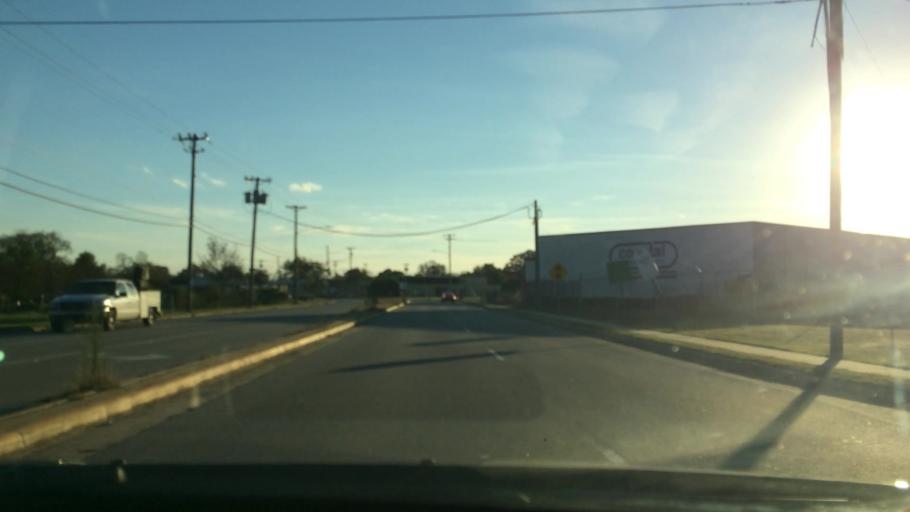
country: US
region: North Carolina
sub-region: Lenoir County
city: Kinston
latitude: 35.2705
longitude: -77.5707
